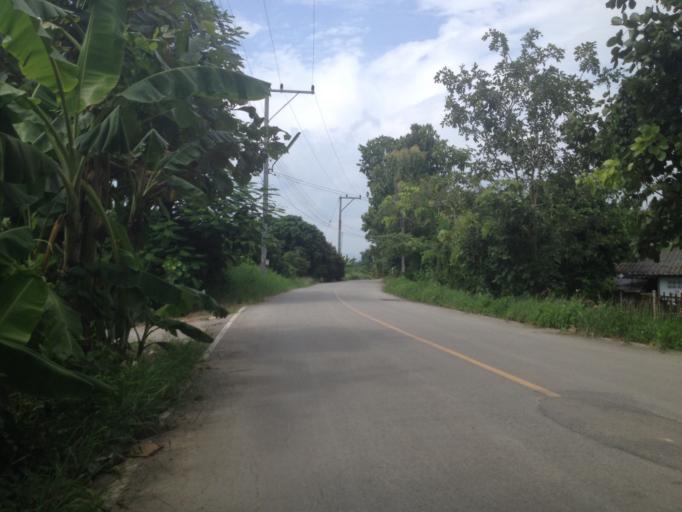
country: TH
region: Chiang Mai
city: Hang Dong
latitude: 18.6656
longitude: 98.9645
